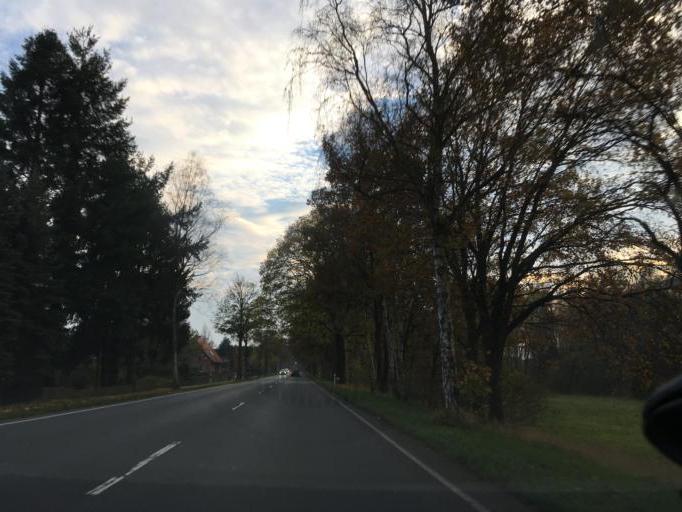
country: DE
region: Lower Saxony
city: Bergen
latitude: 52.7393
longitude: 9.9772
